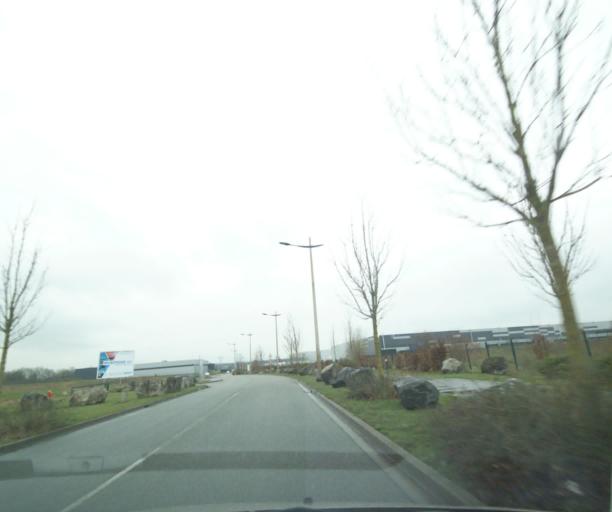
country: FR
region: Nord-Pas-de-Calais
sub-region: Departement du Nord
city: Haulchin
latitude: 50.3331
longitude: 3.4394
